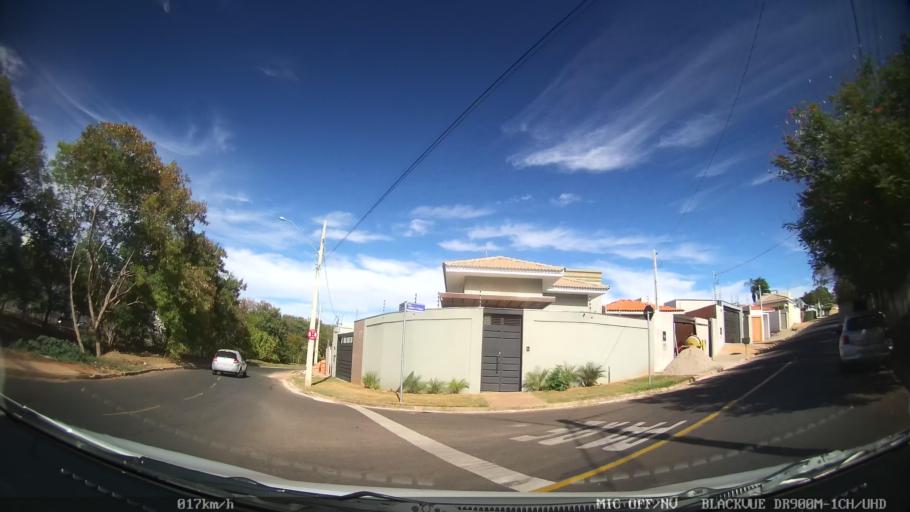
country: BR
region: Sao Paulo
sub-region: Catanduva
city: Catanduva
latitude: -21.1217
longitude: -48.9594
